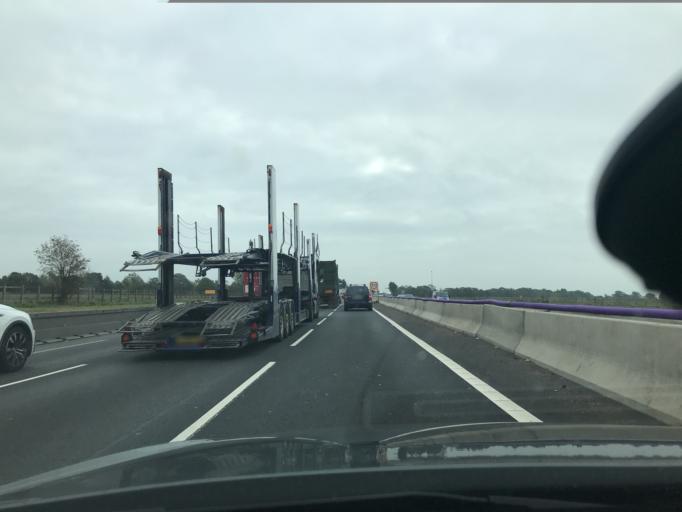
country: GB
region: England
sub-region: Cheshire East
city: Holmes Chapel
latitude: 53.2270
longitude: -2.3944
